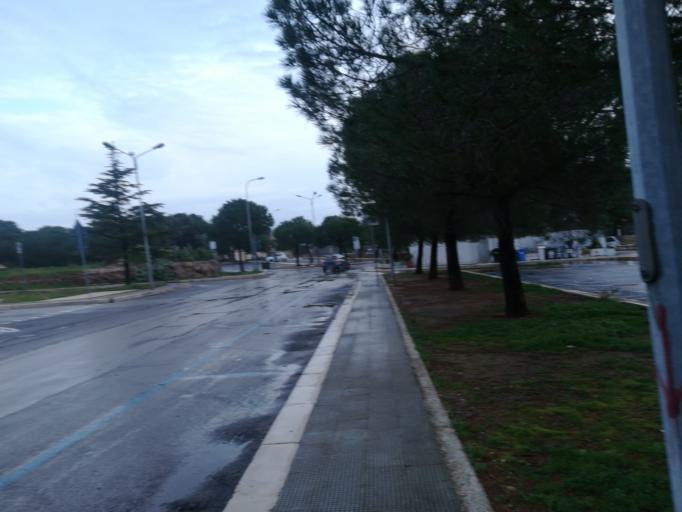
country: IT
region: Apulia
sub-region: Provincia di Bari
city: Polignano a Mare
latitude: 40.9937
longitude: 17.2157
